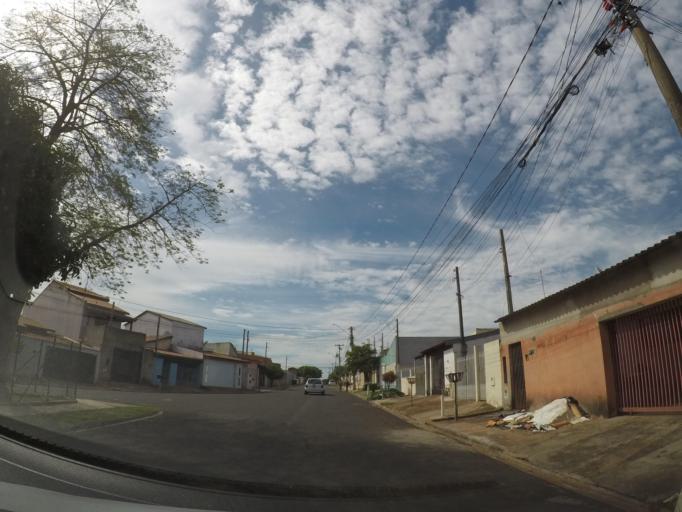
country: BR
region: Sao Paulo
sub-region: Hortolandia
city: Hortolandia
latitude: -22.8303
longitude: -47.1903
